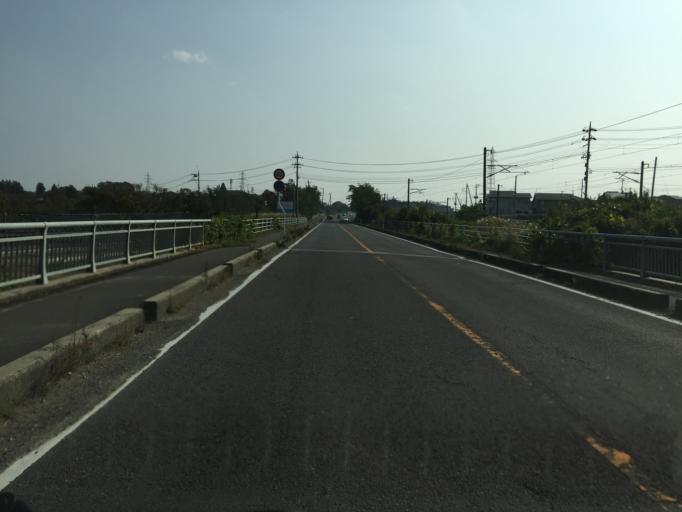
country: JP
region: Fukushima
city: Koriyama
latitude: 37.4418
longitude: 140.3906
